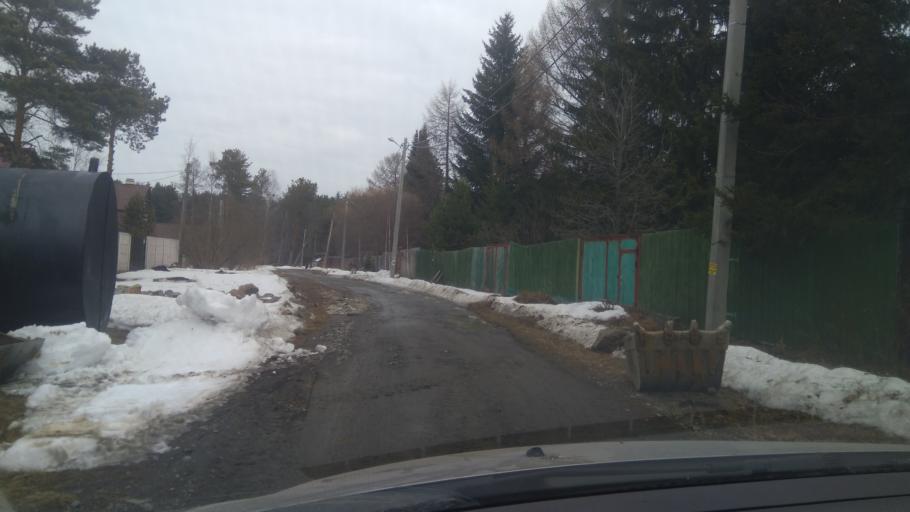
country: RU
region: Sverdlovsk
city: Severka
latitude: 56.8532
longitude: 60.3839
